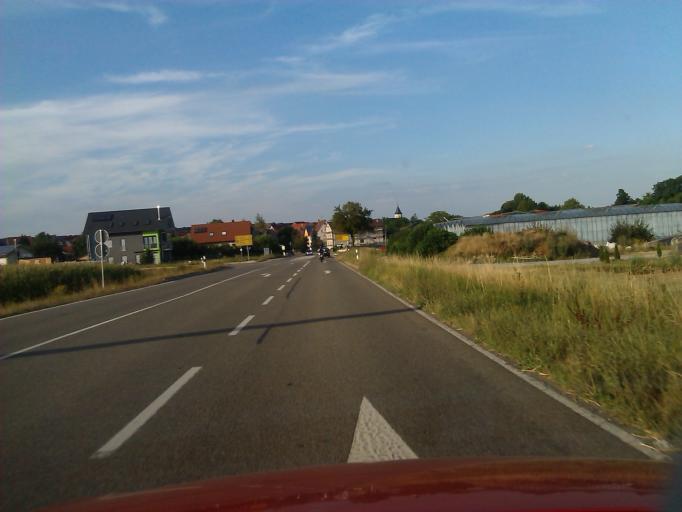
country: DE
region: Baden-Wuerttemberg
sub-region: Regierungsbezirk Stuttgart
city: Gemmingen
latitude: 49.1264
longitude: 9.0035
